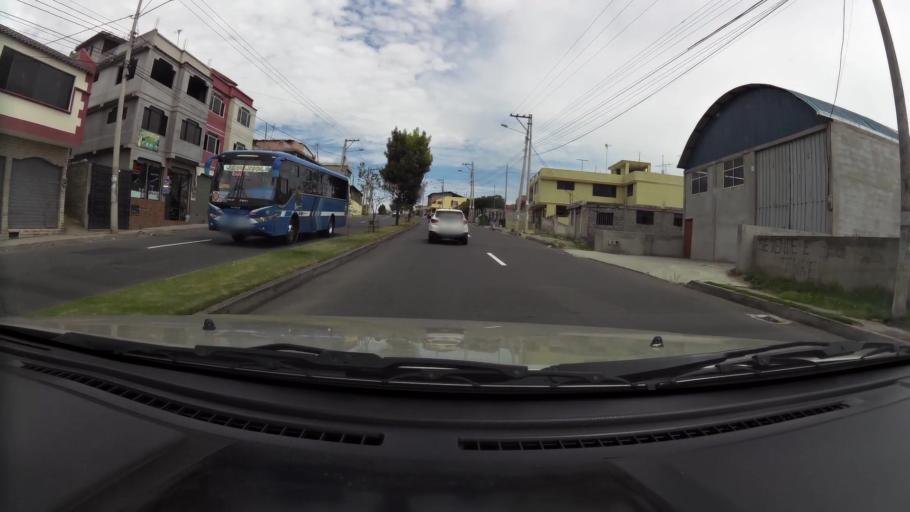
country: EC
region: Tungurahua
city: Pillaro
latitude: -1.1309
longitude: -78.5884
